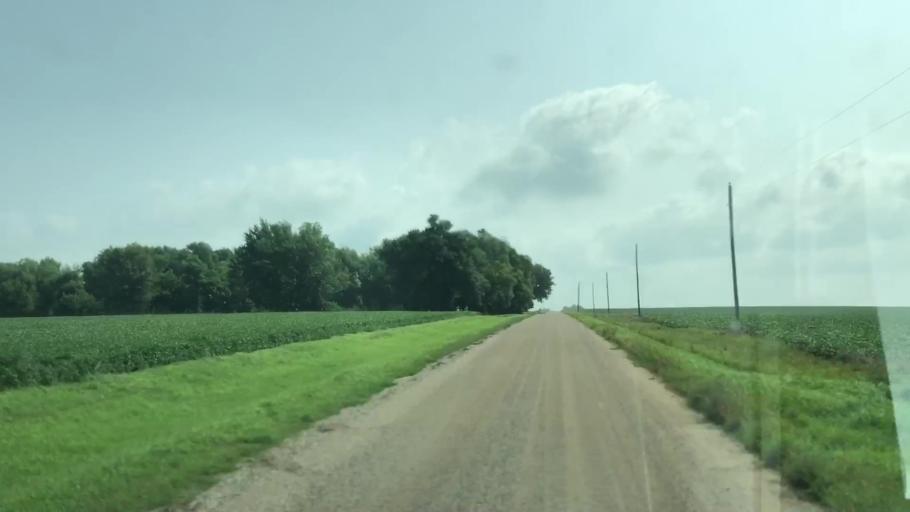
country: US
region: Iowa
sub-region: O'Brien County
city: Sheldon
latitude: 43.2004
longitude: -95.9190
